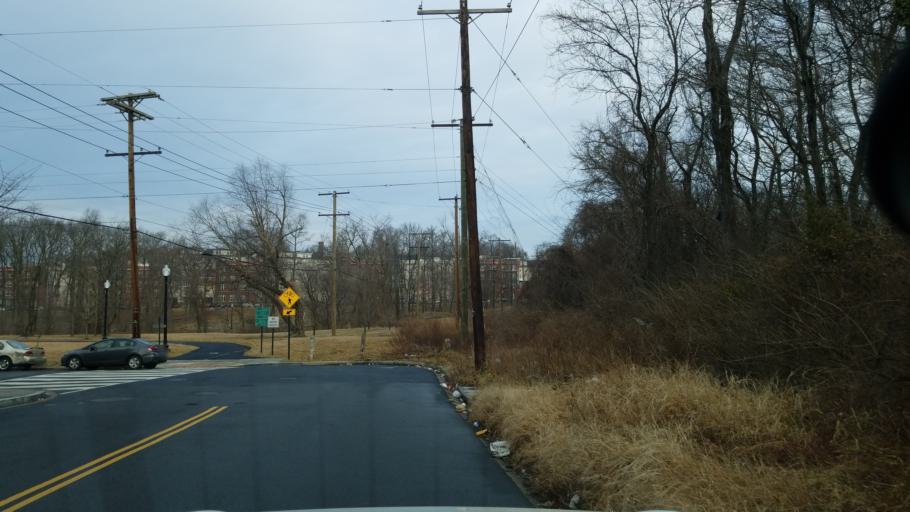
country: US
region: Maryland
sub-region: Prince George's County
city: Glassmanor
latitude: 38.8377
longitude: -76.9882
